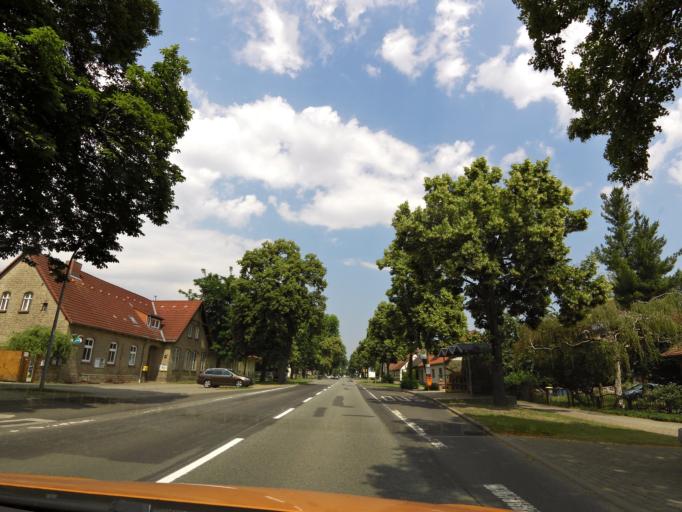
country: DE
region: Brandenburg
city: Wustermark
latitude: 52.4947
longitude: 12.9248
